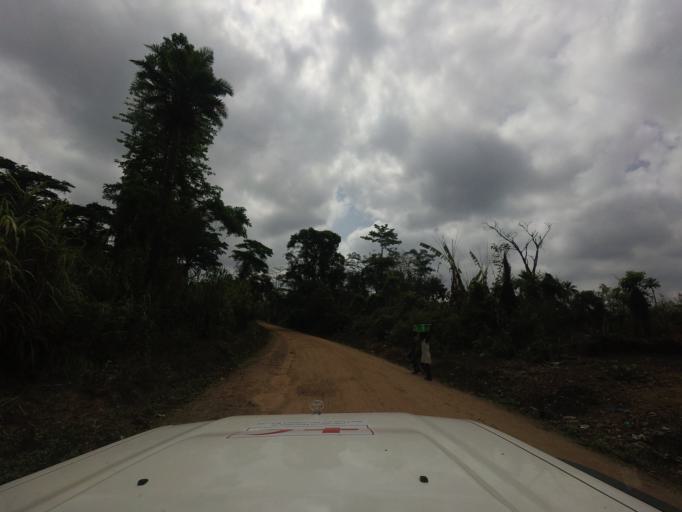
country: LR
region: Lofa
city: Voinjama
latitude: 8.4090
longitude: -9.7155
